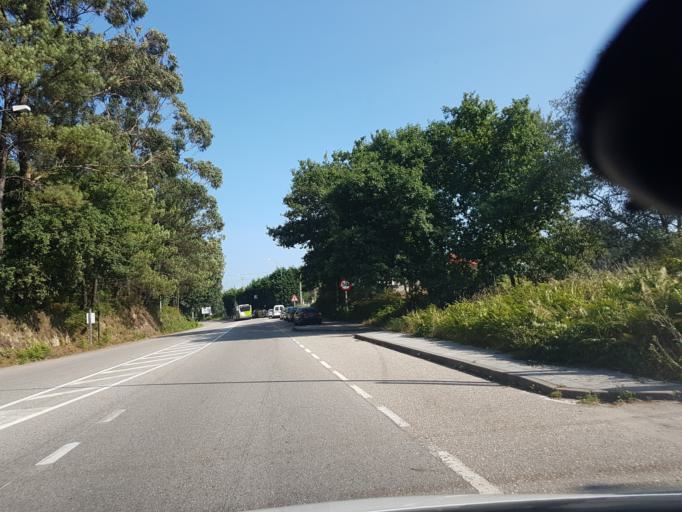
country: ES
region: Galicia
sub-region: Provincia de Pontevedra
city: Redondela
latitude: 42.2298
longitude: -8.6368
